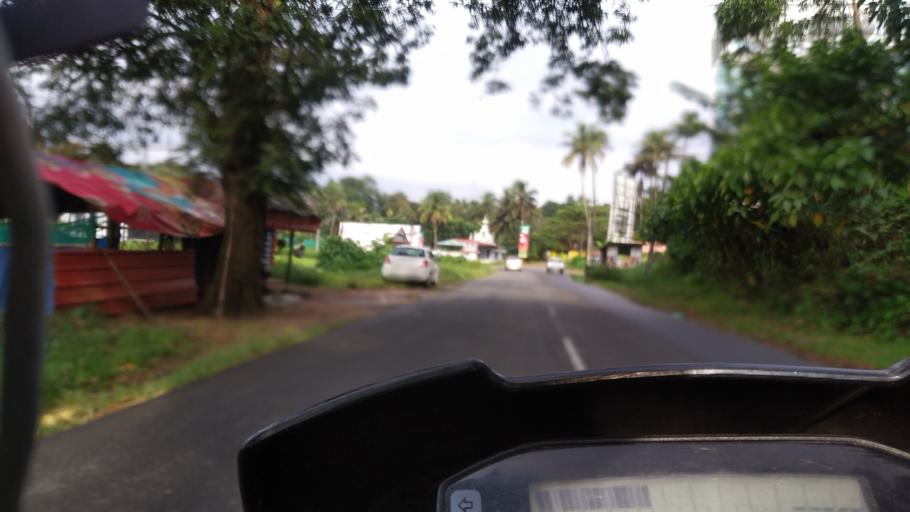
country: IN
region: Kerala
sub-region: Ernakulam
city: Kotamangalam
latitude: 10.0493
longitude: 76.7206
